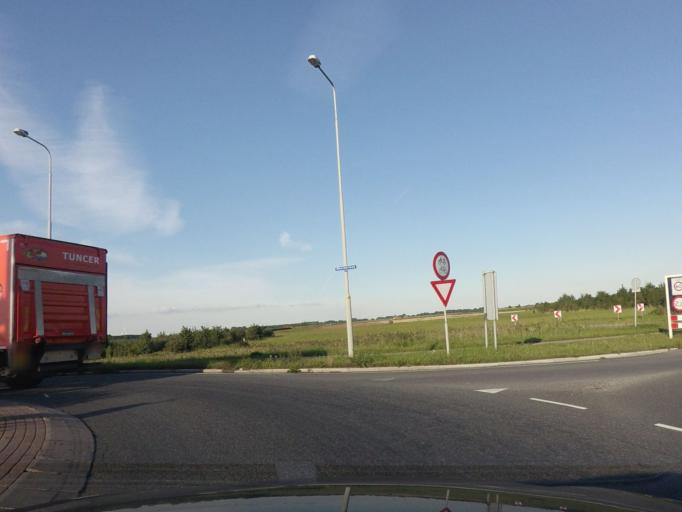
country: NL
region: North Holland
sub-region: Gemeente Beverwijk
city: Beverwijk
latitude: 52.4739
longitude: 4.6852
